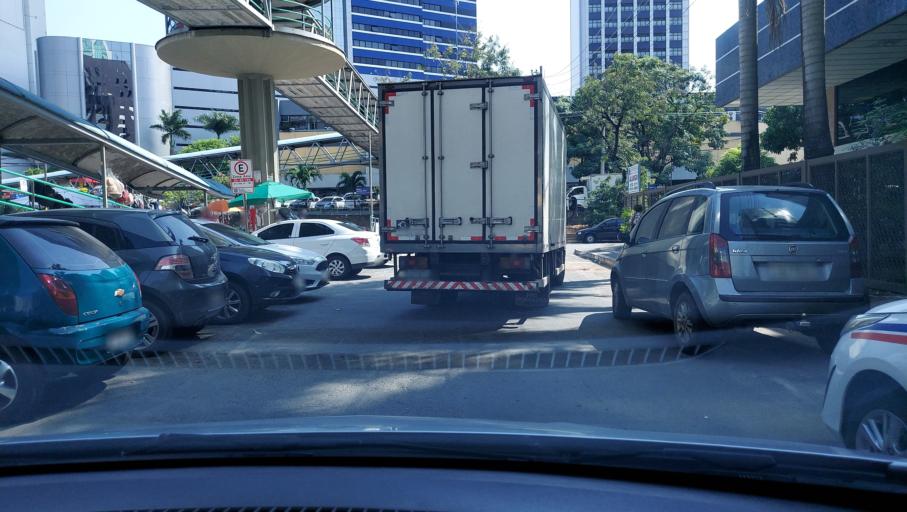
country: BR
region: Bahia
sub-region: Salvador
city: Salvador
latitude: -12.9819
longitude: -38.4544
